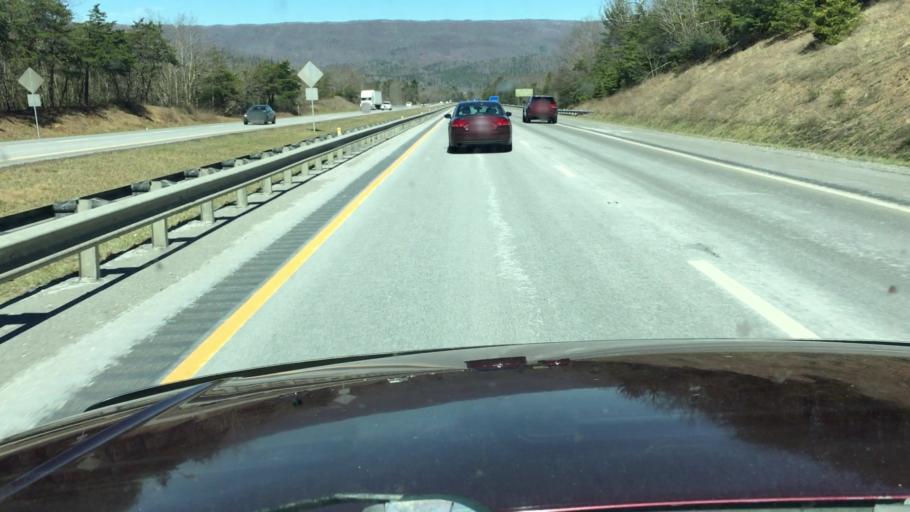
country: US
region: Virginia
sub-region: Bland County
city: Bland
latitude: 37.1449
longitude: -81.1388
